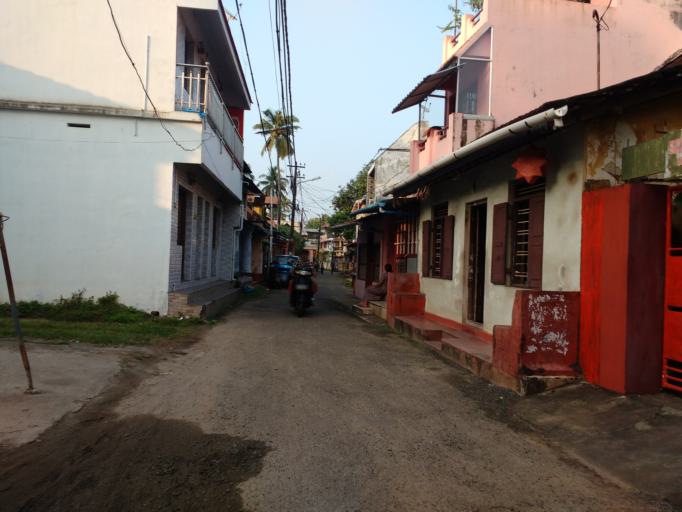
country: IN
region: Kerala
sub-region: Ernakulam
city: Cochin
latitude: 9.9584
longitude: 76.2502
